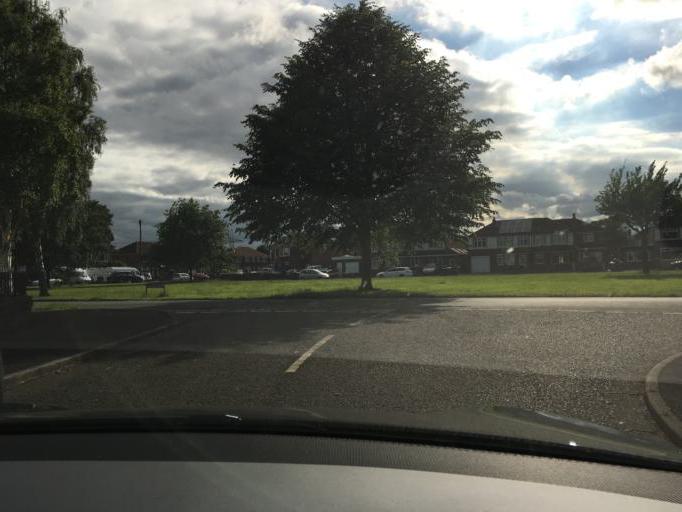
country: GB
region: England
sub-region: Trafford
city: Urmston
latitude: 53.4384
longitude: -2.3658
